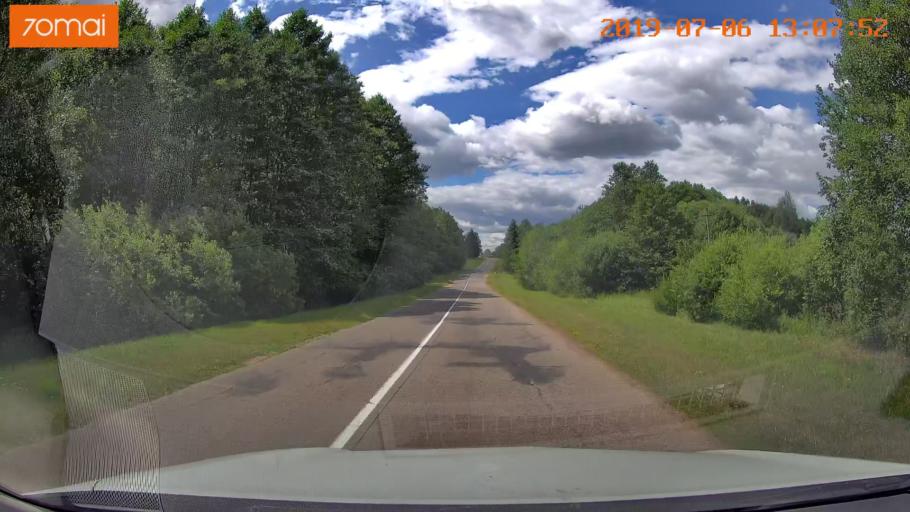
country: BY
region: Minsk
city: Enyerhyetykaw
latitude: 53.6721
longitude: 27.0341
